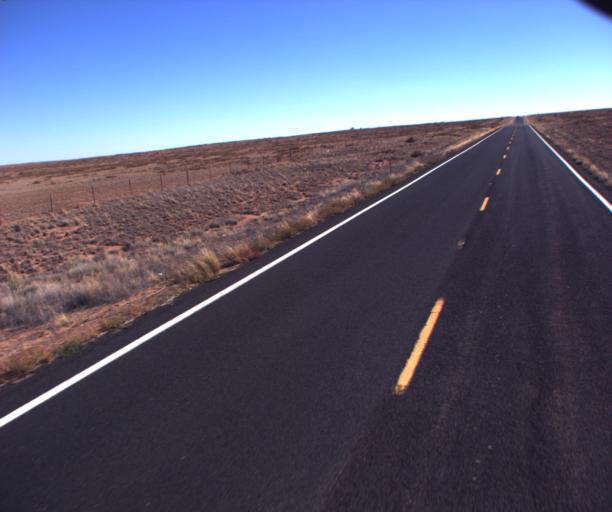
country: US
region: Arizona
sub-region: Coconino County
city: Tuba City
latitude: 36.0142
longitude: -111.0876
